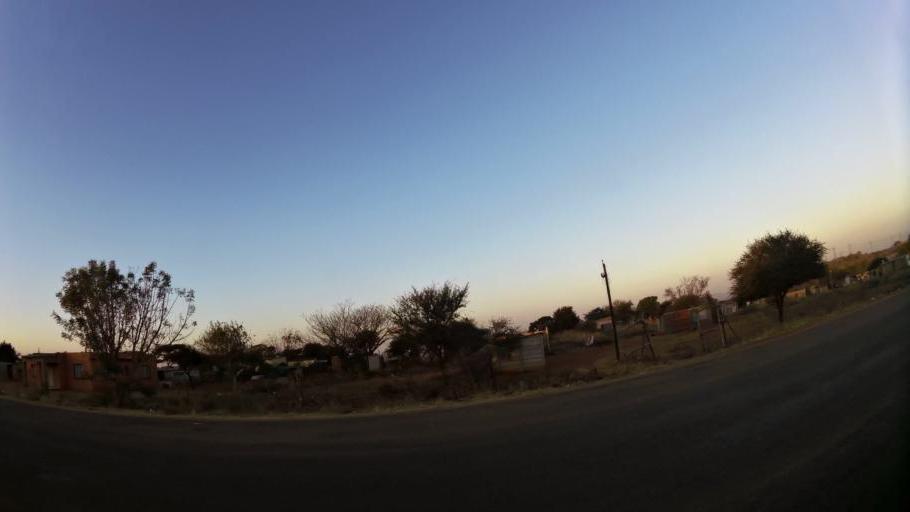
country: ZA
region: North-West
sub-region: Bojanala Platinum District Municipality
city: Rustenburg
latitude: -25.6257
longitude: 27.1978
